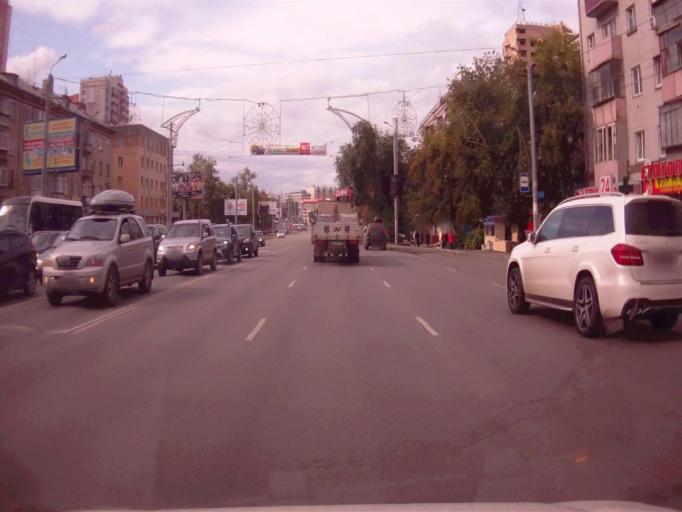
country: RU
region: Chelyabinsk
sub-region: Gorod Chelyabinsk
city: Chelyabinsk
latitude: 55.1449
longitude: 61.3860
